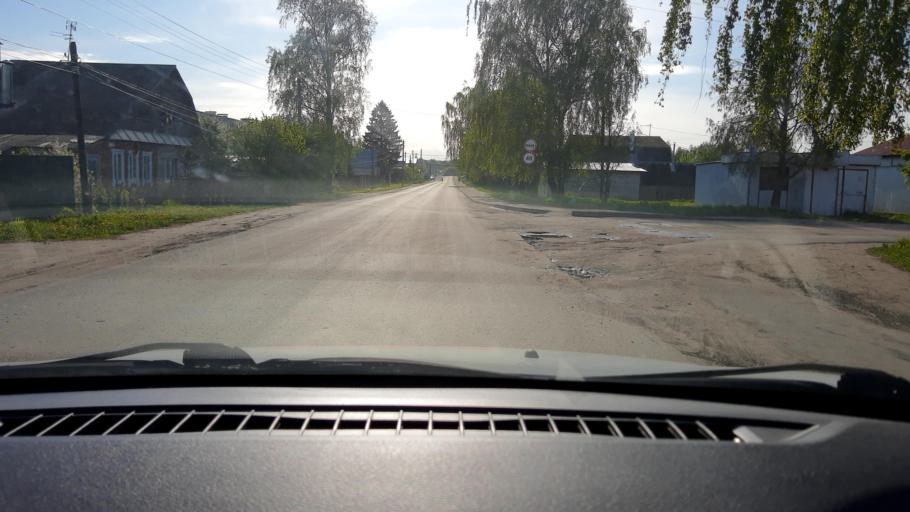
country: RU
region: Nizjnij Novgorod
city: Burevestnik
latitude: 56.1438
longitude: 43.7855
